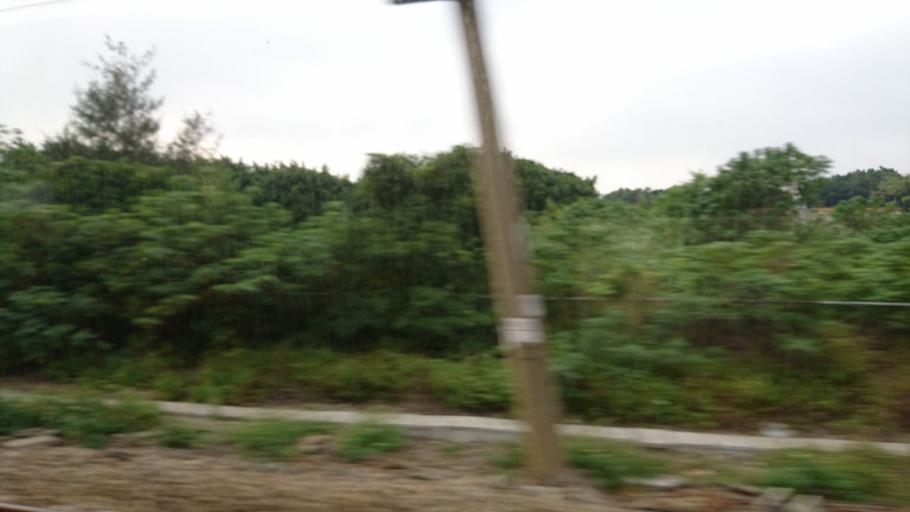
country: TW
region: Taiwan
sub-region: Hsinchu
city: Zhubei
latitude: 24.8433
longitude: 121.0124
